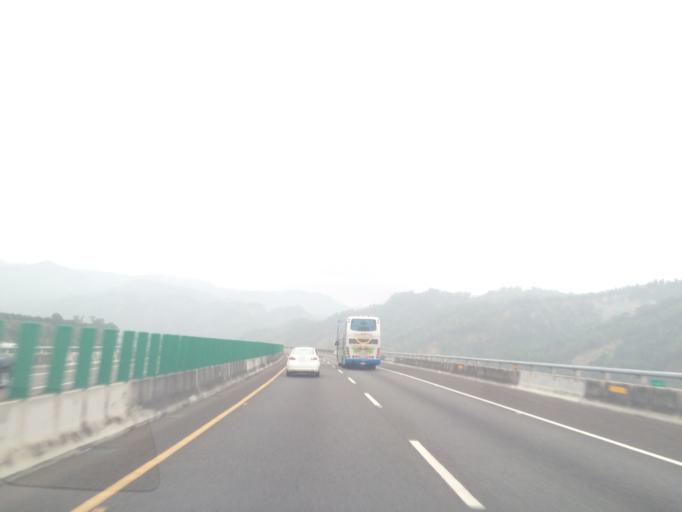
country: TW
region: Taiwan
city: Zhongxing New Village
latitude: 23.9862
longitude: 120.7576
